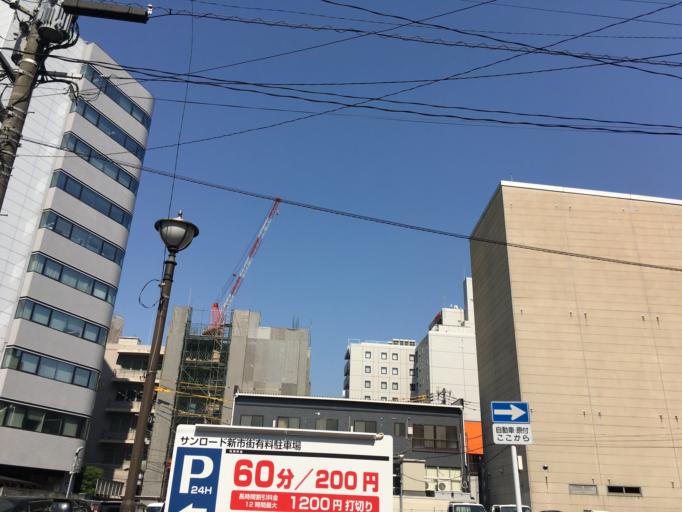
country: JP
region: Kumamoto
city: Kumamoto
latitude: 32.7985
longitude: 130.7065
